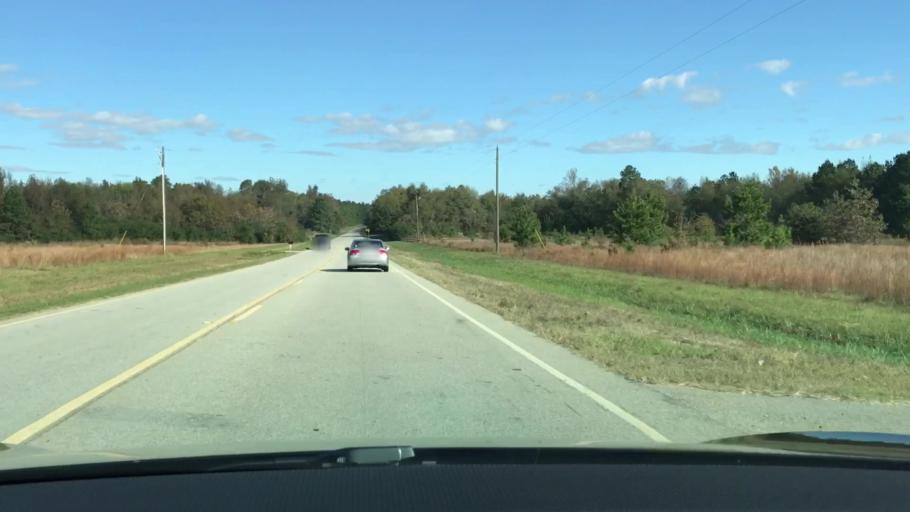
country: US
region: Georgia
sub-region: Jefferson County
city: Wrens
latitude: 33.2325
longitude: -82.4586
